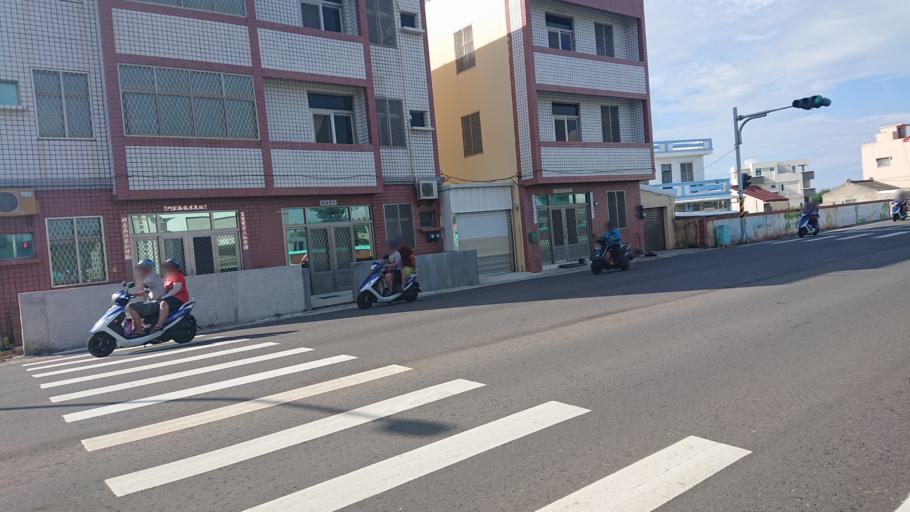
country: TW
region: Taiwan
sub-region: Penghu
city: Ma-kung
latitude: 23.5268
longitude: 119.5886
